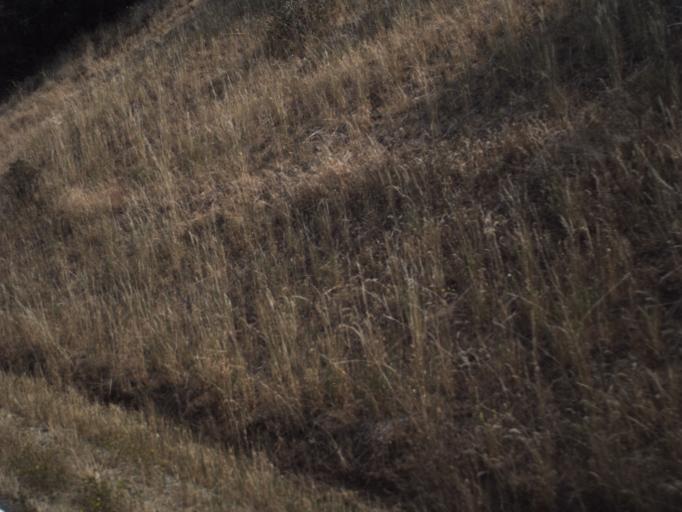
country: US
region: Utah
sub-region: Summit County
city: Summit Park
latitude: 40.8082
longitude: -111.6779
